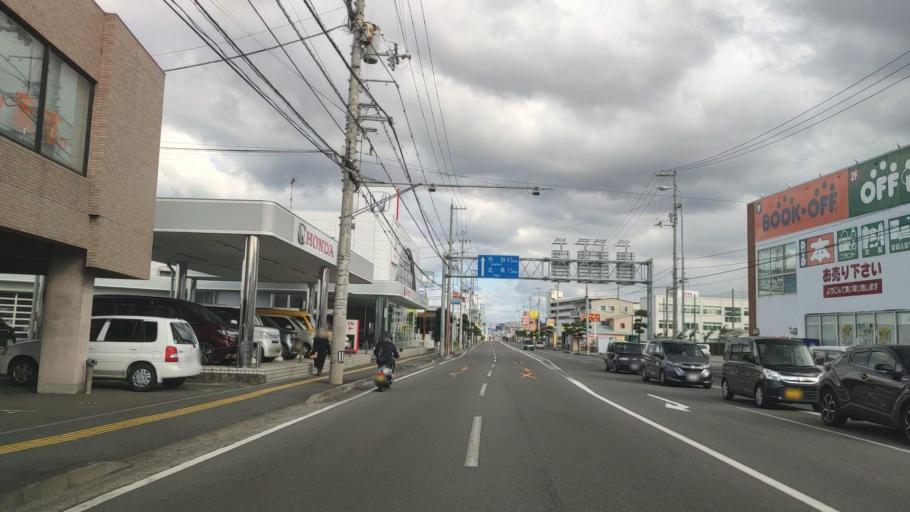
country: JP
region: Ehime
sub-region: Shikoku-chuo Shi
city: Matsuyama
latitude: 33.8553
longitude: 132.7480
